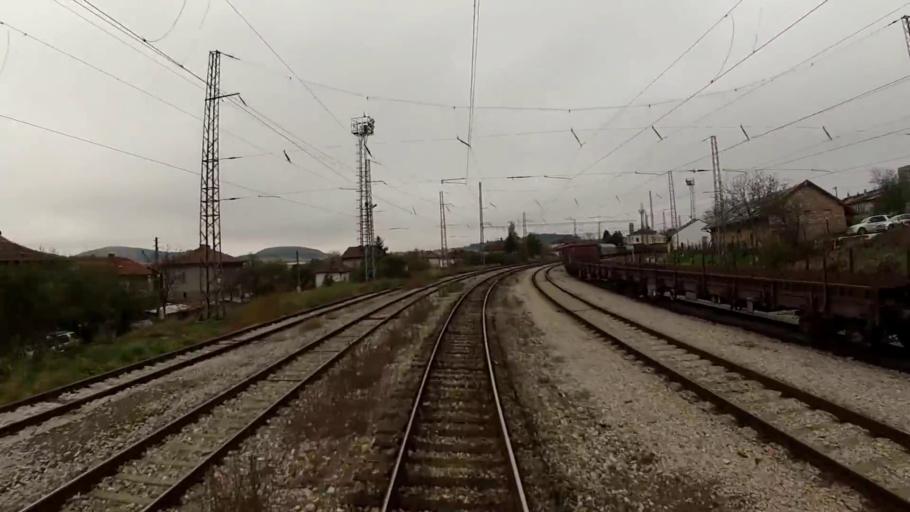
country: BG
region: Sofiya
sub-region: Obshtina Dragoman
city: Dragoman
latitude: 42.9301
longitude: 22.9315
